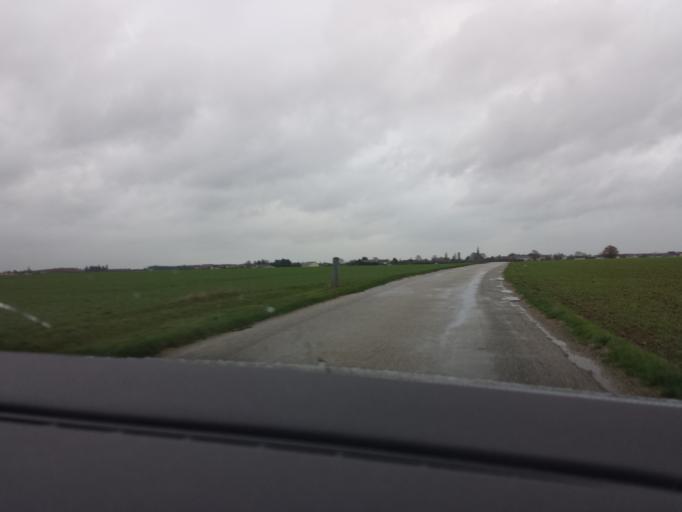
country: FR
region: Haute-Normandie
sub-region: Departement de l'Eure
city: Evreux
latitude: 49.0052
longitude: 1.2046
